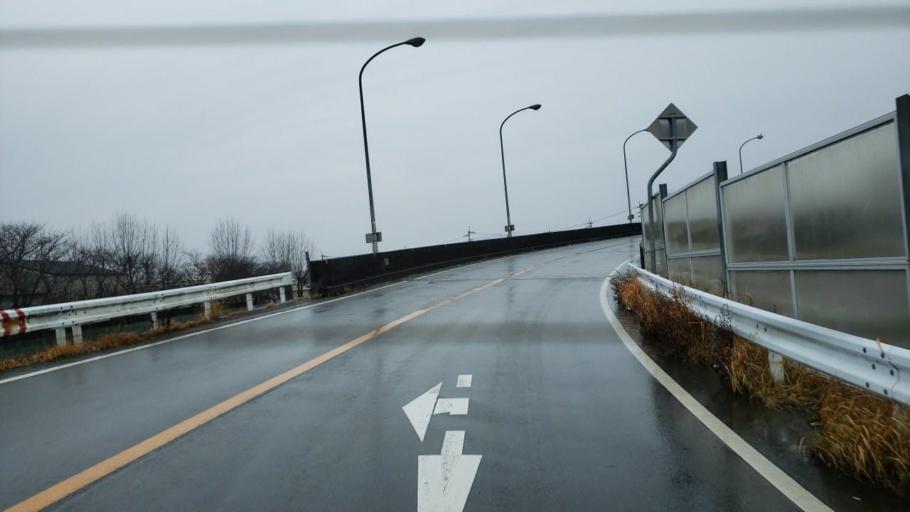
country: JP
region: Tokushima
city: Kamojimacho-jogejima
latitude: 34.0626
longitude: 134.2814
